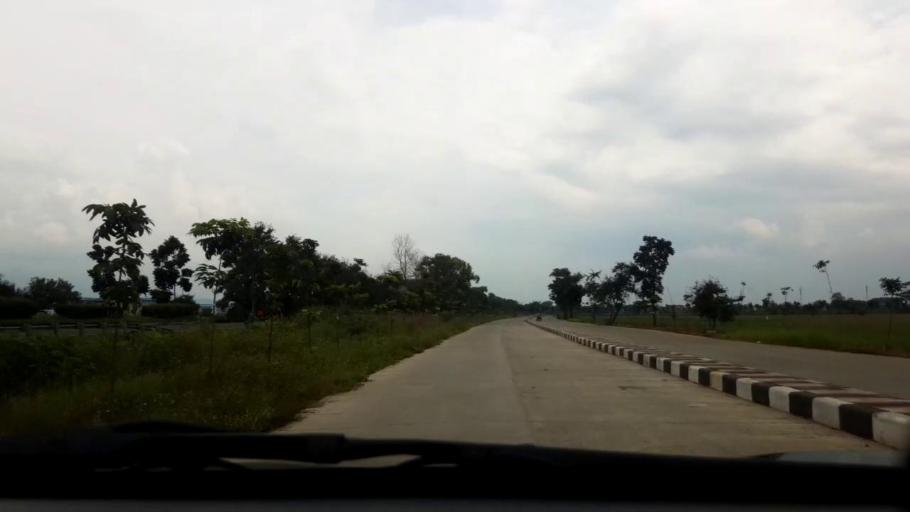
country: ID
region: West Java
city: Cileunyi
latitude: -6.9629
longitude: 107.7129
